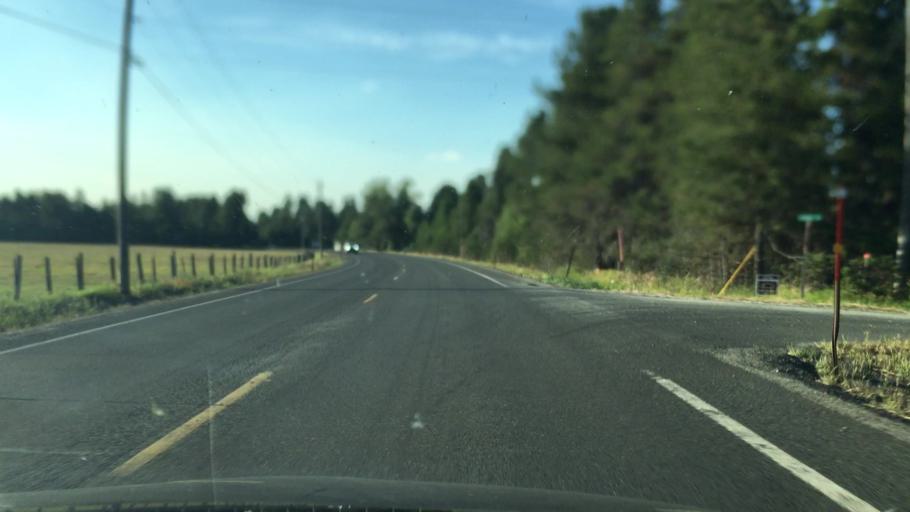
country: US
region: Idaho
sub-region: Valley County
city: McCall
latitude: 44.8227
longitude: -116.0782
